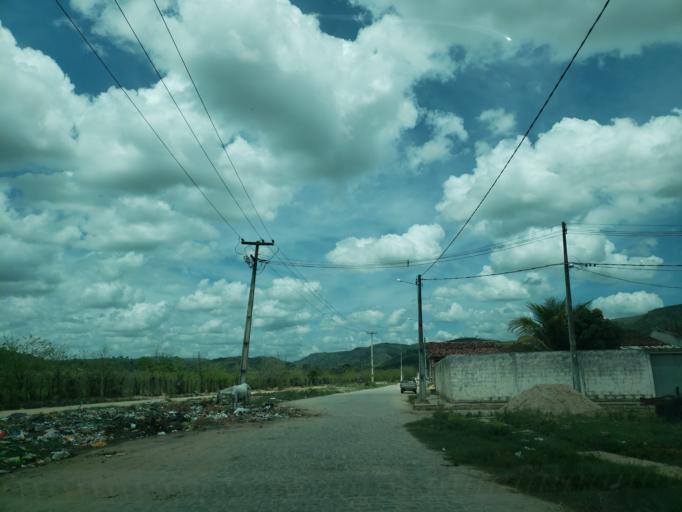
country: BR
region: Alagoas
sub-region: Uniao Dos Palmares
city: Uniao dos Palmares
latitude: -9.1491
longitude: -36.0111
